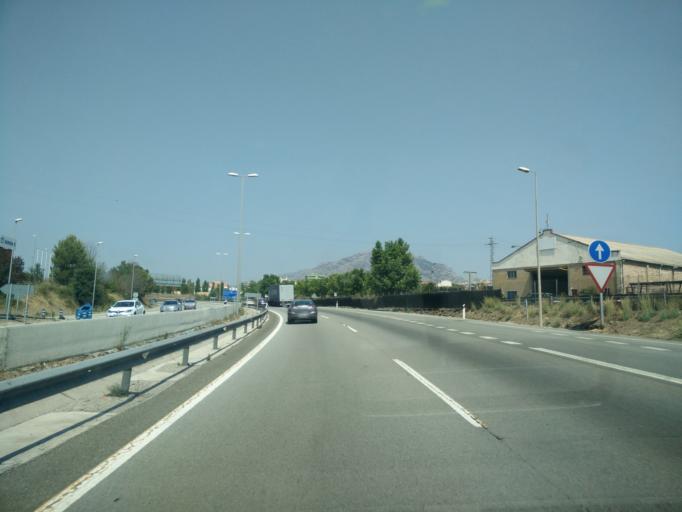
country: ES
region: Catalonia
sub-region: Provincia de Barcelona
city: Esparreguera
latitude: 41.5294
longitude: 1.8786
